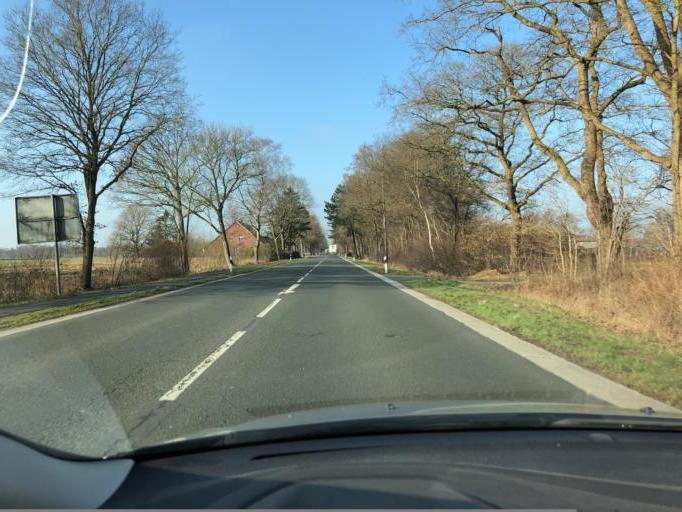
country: DE
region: Lower Saxony
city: Westerstede
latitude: 53.2934
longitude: 7.8599
